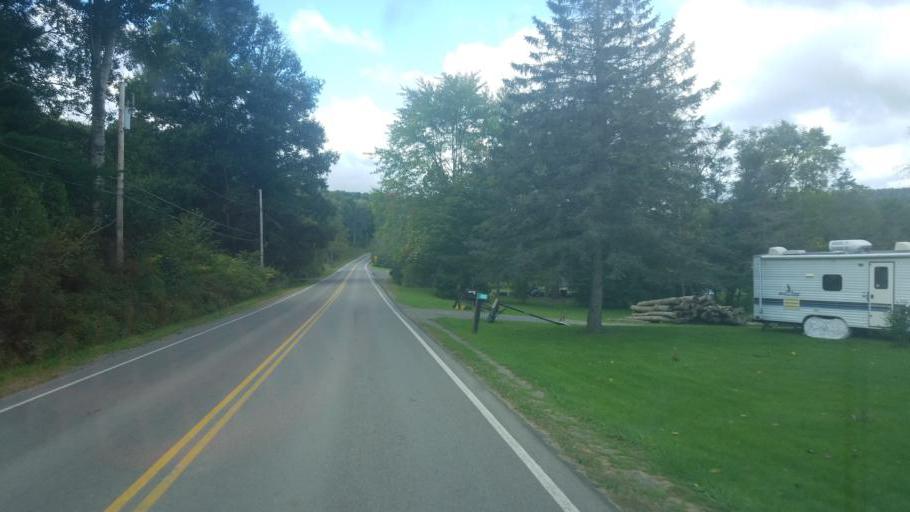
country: US
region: New York
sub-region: Allegany County
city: Cuba
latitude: 42.1468
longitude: -78.3073
